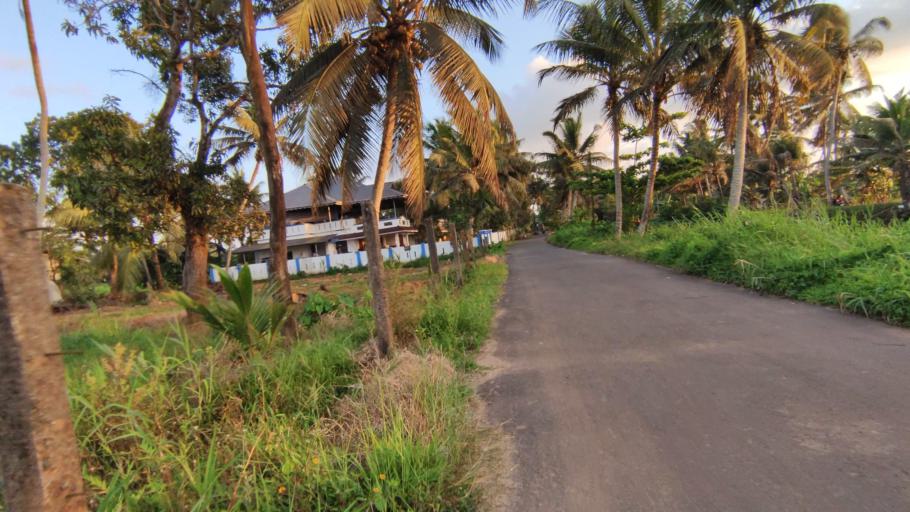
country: IN
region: Kerala
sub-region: Kottayam
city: Kottayam
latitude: 9.5884
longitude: 76.4482
